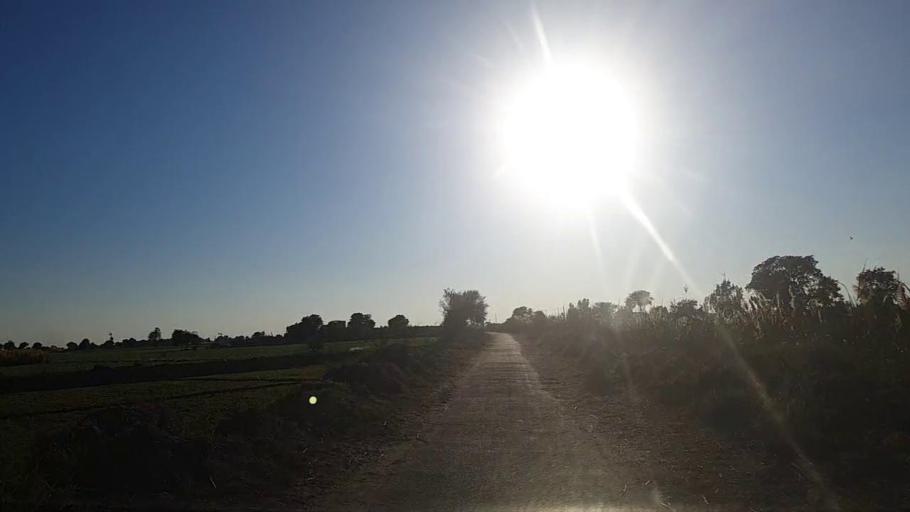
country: PK
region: Sindh
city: Sanghar
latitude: 26.1369
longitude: 68.9446
